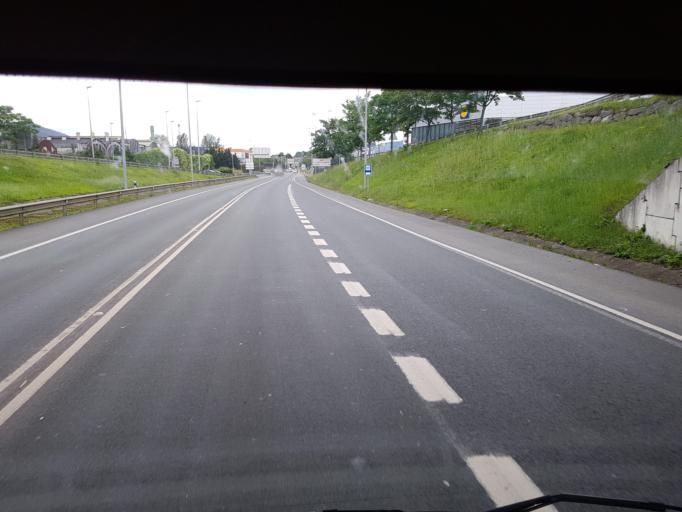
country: ES
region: Basque Country
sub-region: Bizkaia
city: Durango
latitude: 43.1762
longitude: -2.6436
